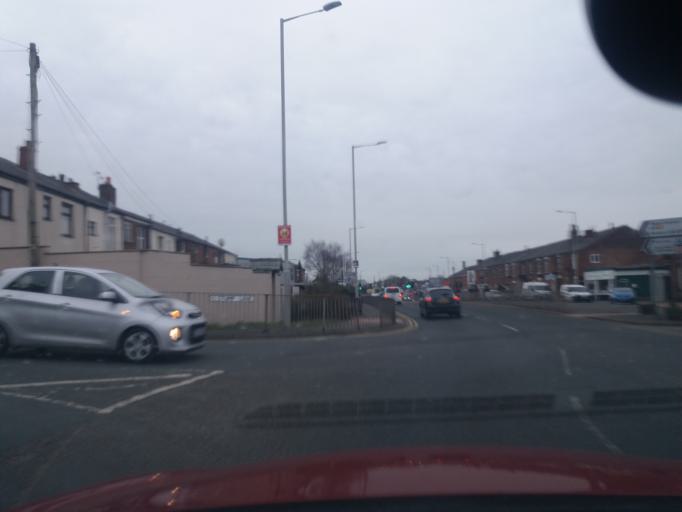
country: GB
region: England
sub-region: Lancashire
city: Chorley
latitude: 53.6561
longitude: -2.6290
